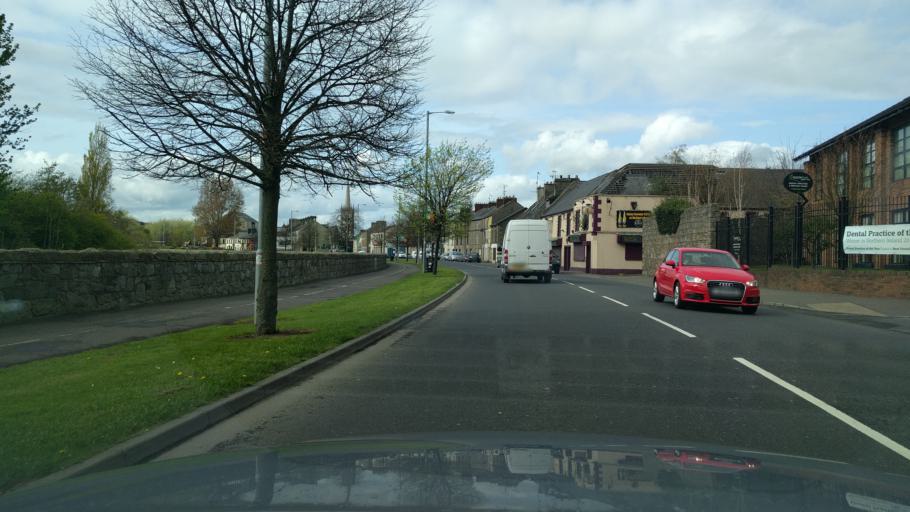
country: GB
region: Northern Ireland
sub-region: Newry and Mourne District
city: Newry
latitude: 54.1691
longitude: -6.3348
